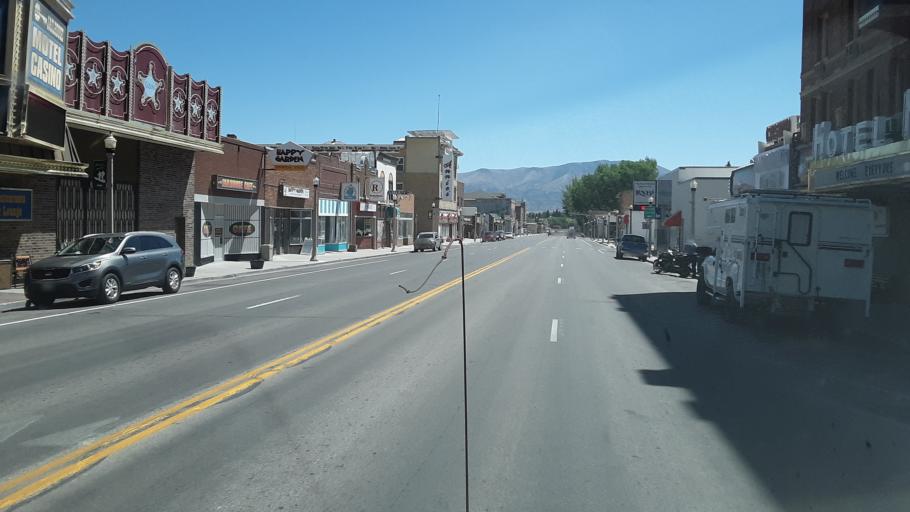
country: US
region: Nevada
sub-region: White Pine County
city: Ely
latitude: 39.2480
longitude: -114.8929
